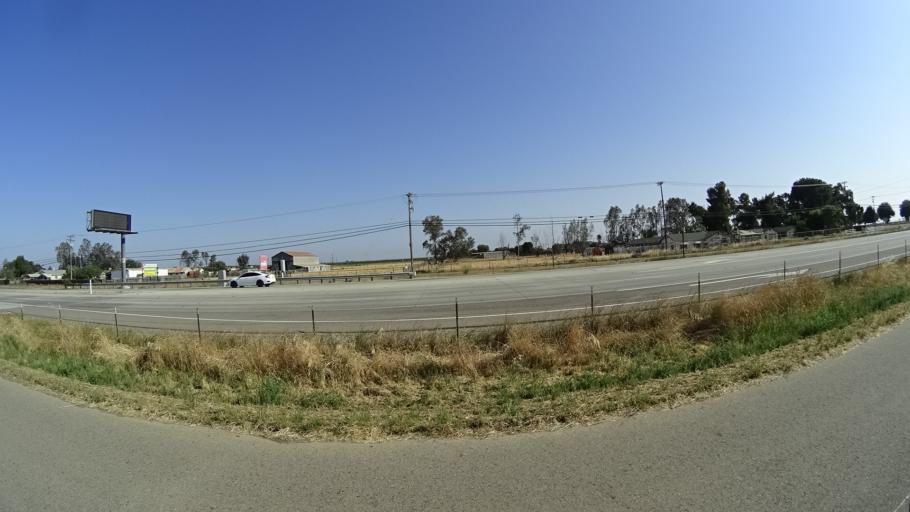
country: US
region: California
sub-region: Kings County
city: Home Garden
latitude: 36.3275
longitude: -119.5854
